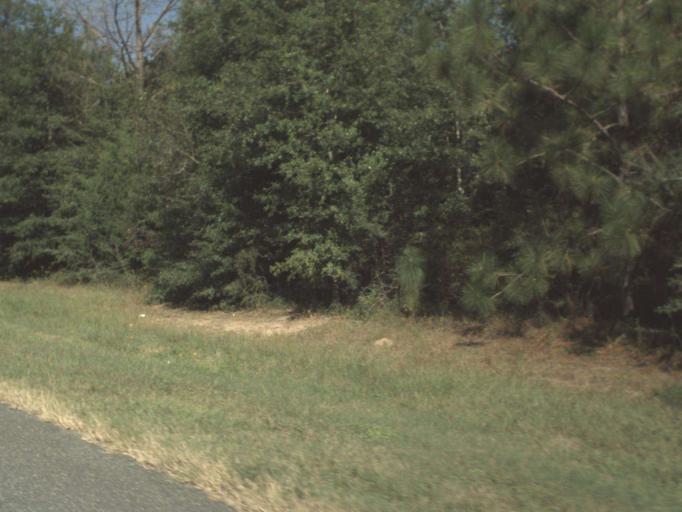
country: US
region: Florida
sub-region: Okaloosa County
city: Crestview
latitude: 30.8457
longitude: -86.5291
